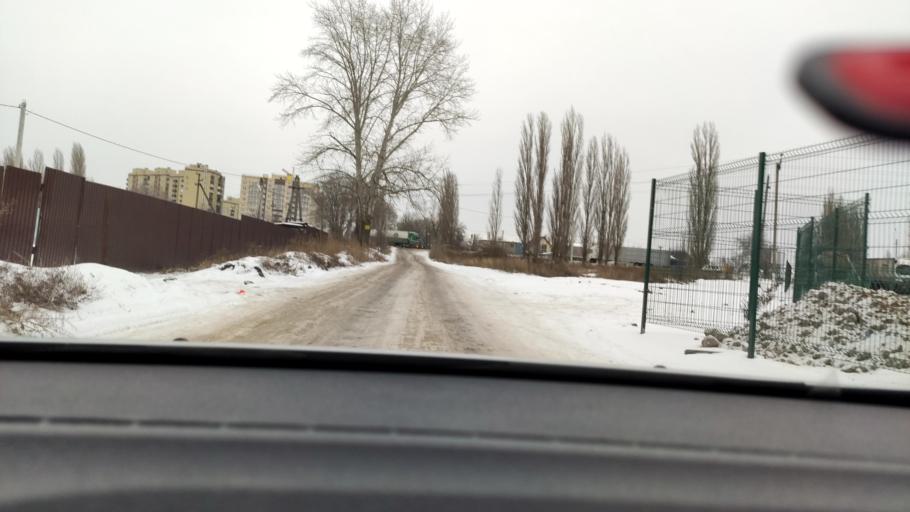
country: RU
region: Voronezj
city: Semiluki
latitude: 51.6934
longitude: 38.9968
